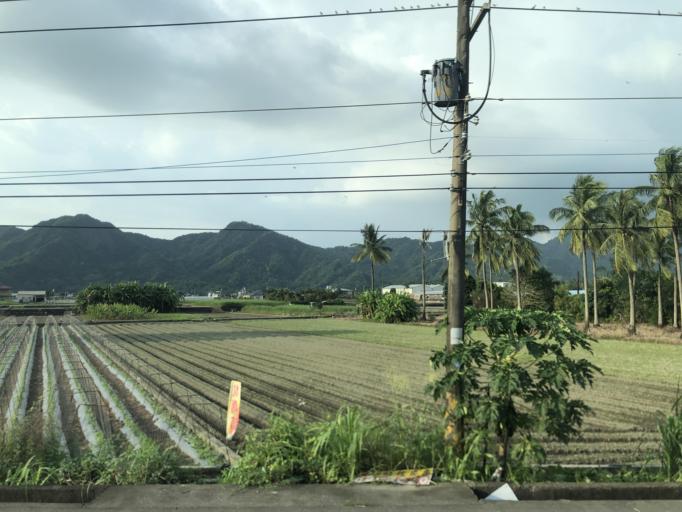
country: TW
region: Taiwan
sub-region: Pingtung
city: Pingtung
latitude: 22.8864
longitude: 120.5201
